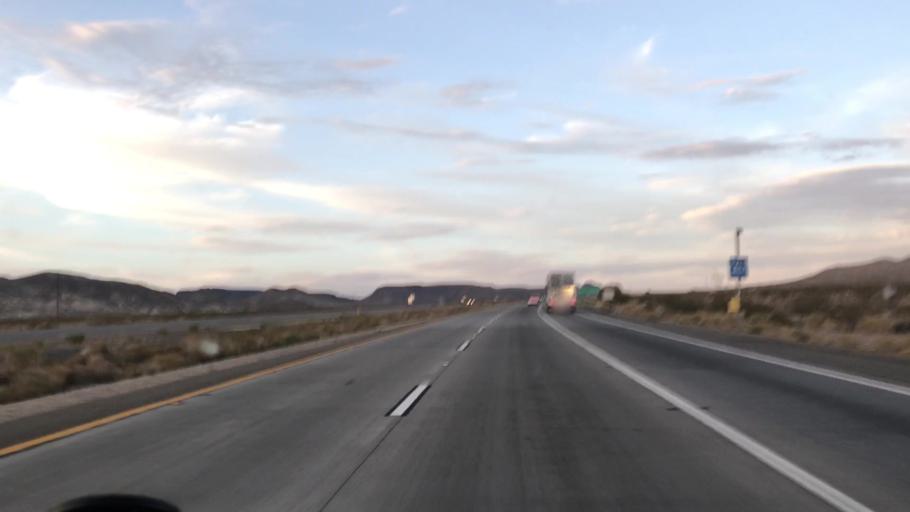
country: US
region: Nevada
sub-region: Clark County
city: Sandy Valley
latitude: 35.3672
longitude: -115.9130
